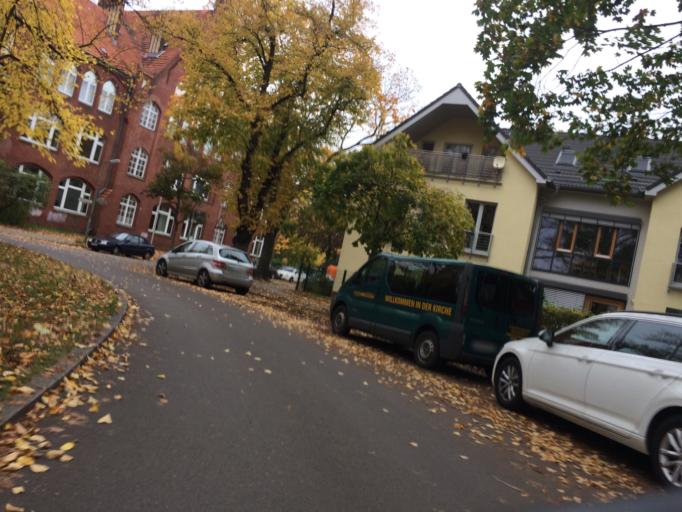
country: DE
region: Berlin
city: Wilhelmsruh
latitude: 52.5695
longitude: 13.3758
